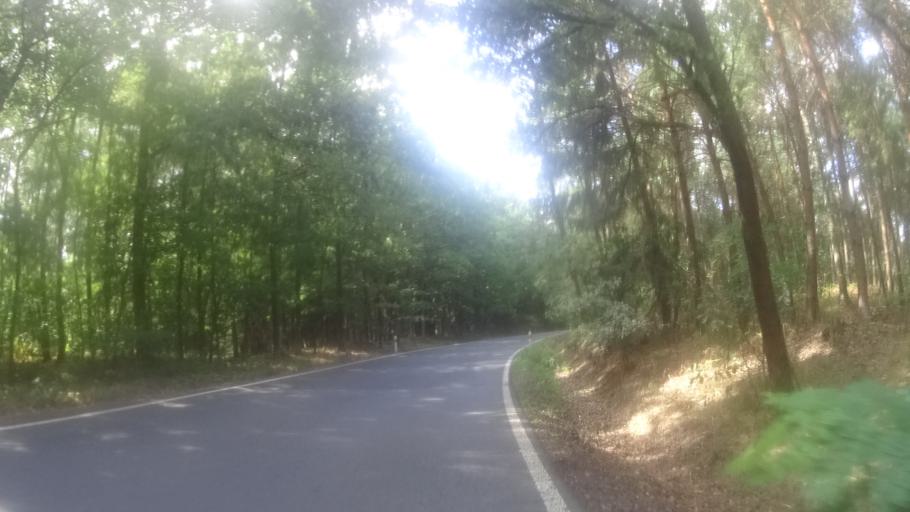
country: CZ
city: Borohradek
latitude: 50.0878
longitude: 16.1076
